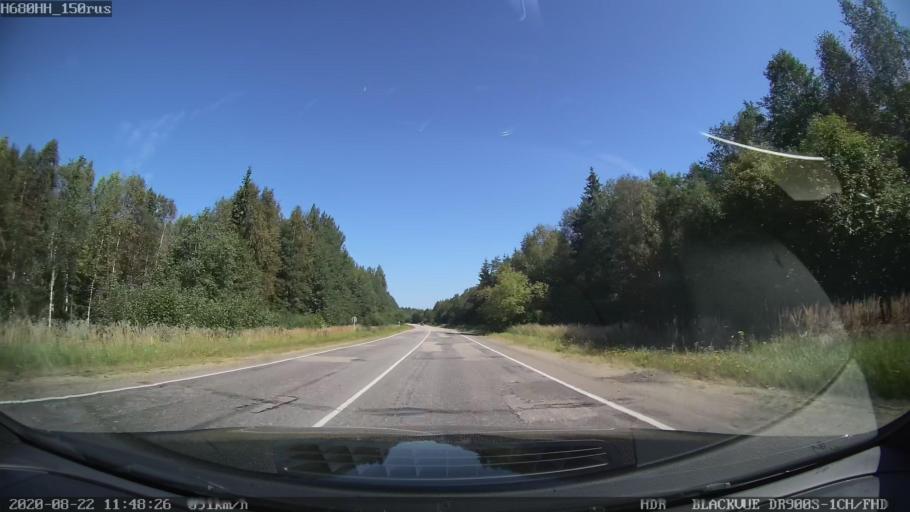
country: RU
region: Tverskaya
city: Sakharovo
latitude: 57.0629
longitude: 36.1033
